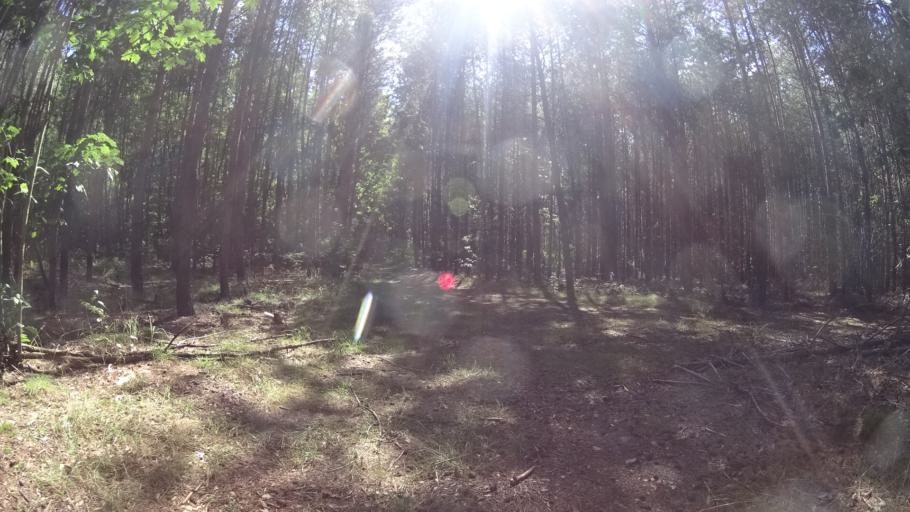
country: PL
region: Masovian Voivodeship
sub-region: Powiat grojecki
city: Mogielnica
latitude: 51.6736
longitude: 20.7491
